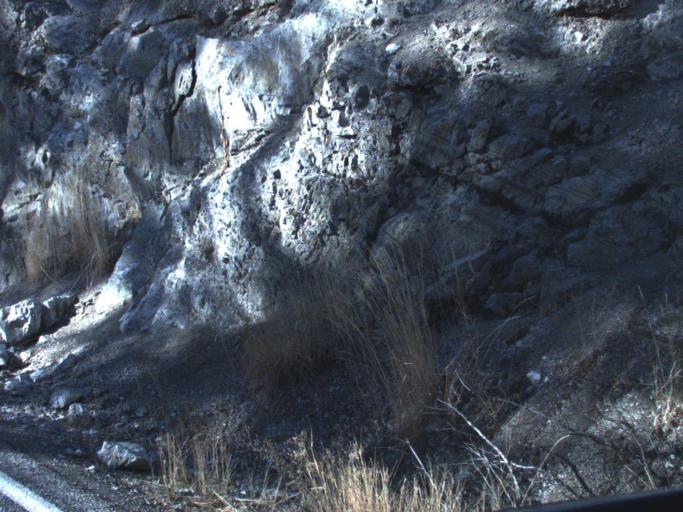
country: CA
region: British Columbia
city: Grand Forks
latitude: 48.9079
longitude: -118.5705
